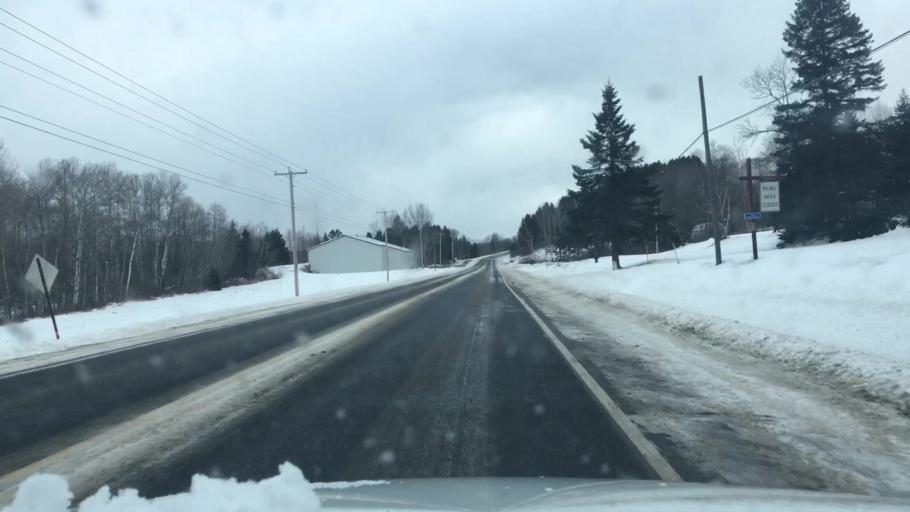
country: US
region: Maine
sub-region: Aroostook County
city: Madawaska
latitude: 47.3273
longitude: -68.1813
